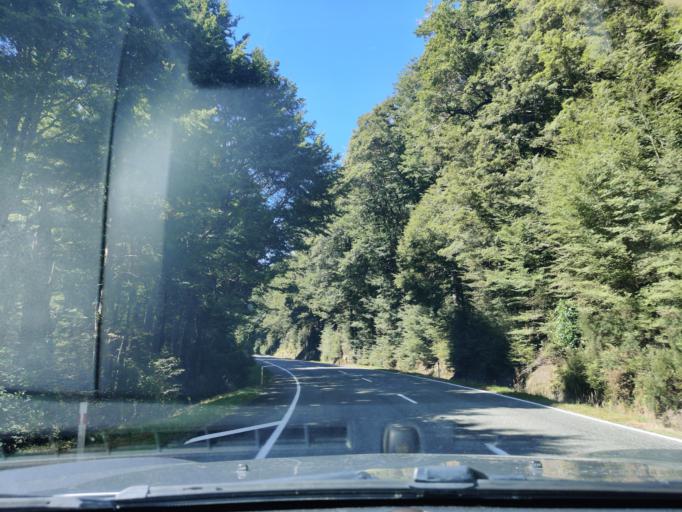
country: NZ
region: Canterbury
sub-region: Hurunui District
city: Amberley
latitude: -42.3793
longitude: 172.3442
